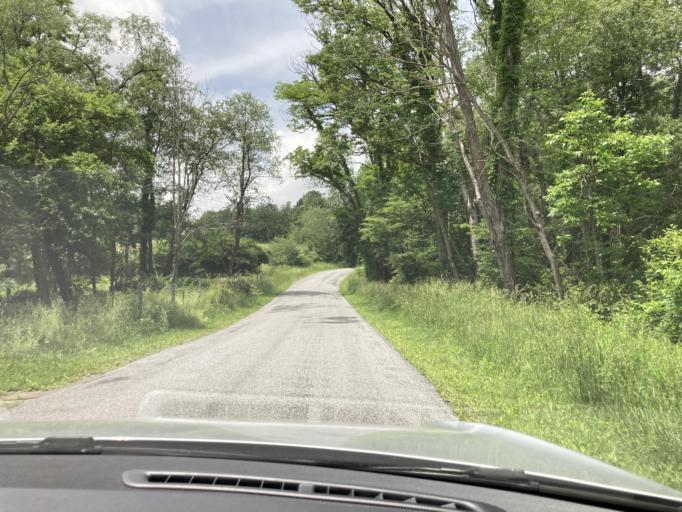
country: US
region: Pennsylvania
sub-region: Somerset County
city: Boswell
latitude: 40.1700
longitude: -79.0931
